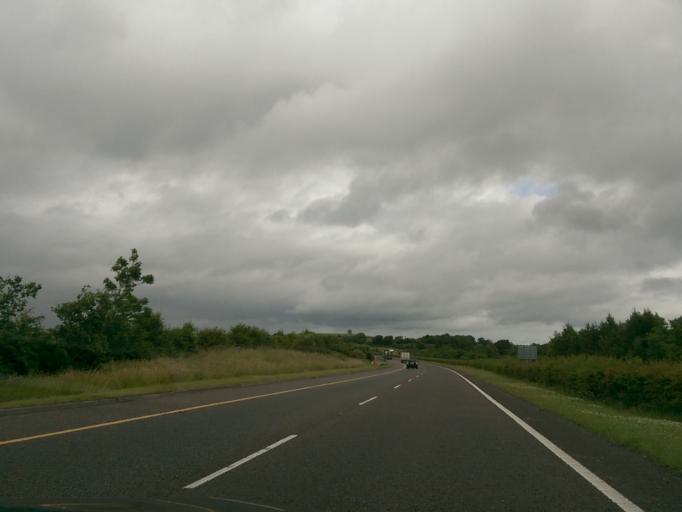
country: IE
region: Munster
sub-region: An Clar
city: Newmarket on Fergus
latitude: 52.7670
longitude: -8.9177
